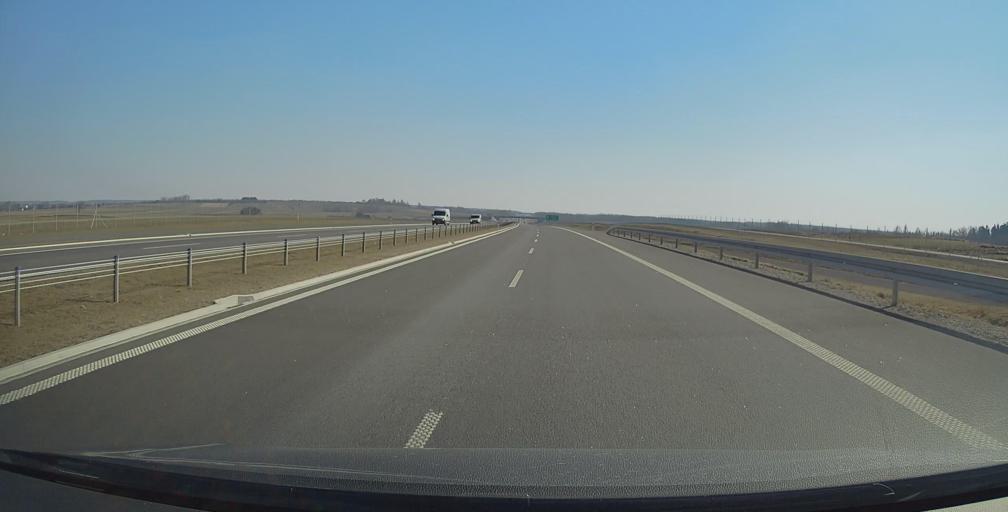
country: PL
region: Lublin Voivodeship
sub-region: Powiat janowski
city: Modliborzyce
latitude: 50.7433
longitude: 22.3053
